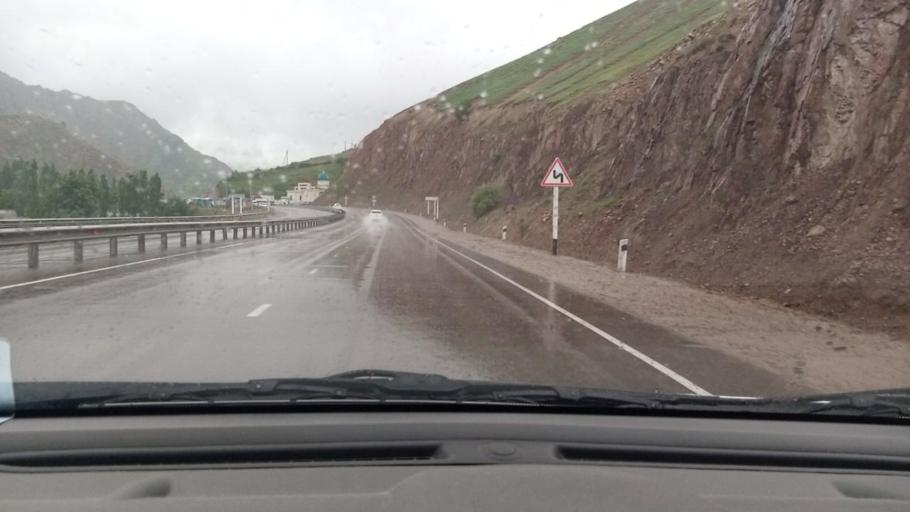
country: UZ
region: Toshkent
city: Angren
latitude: 41.1088
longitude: 70.3358
